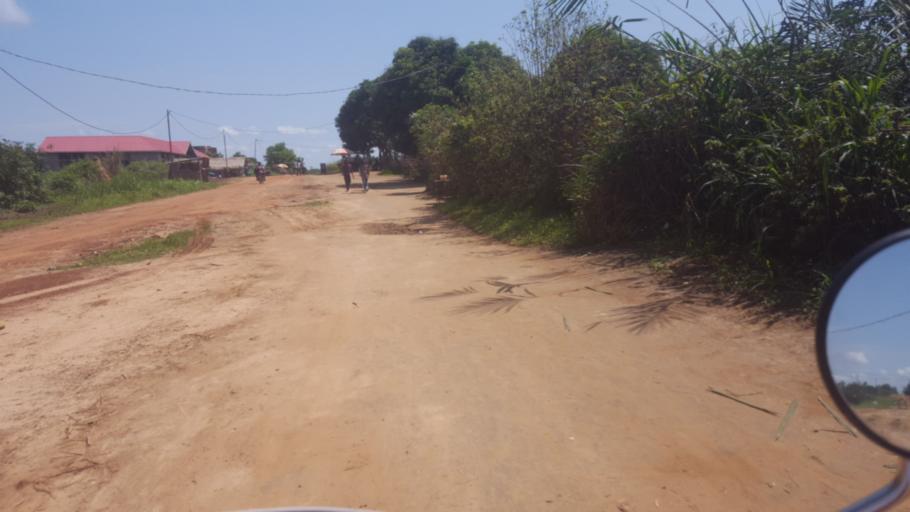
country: CD
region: Bandundu
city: Bandundu
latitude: -3.2916
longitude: 17.3782
